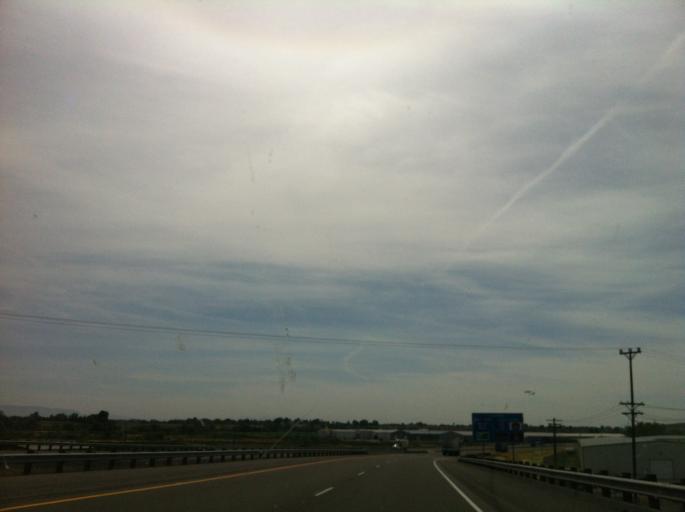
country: US
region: Oregon
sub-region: Malheur County
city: Ontario
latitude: 44.0360
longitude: -116.9589
